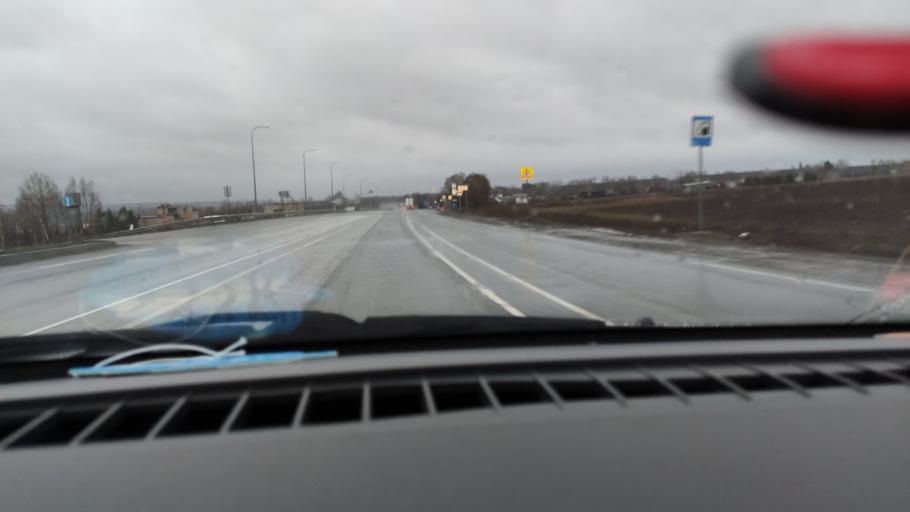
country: RU
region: Tatarstan
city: Mendeleyevsk
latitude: 56.0339
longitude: 52.3811
